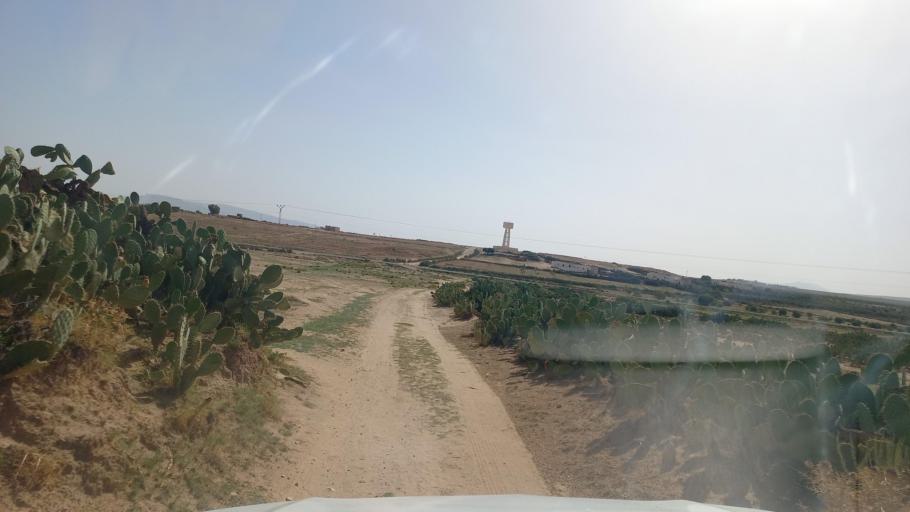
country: TN
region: Al Qasrayn
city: Sbiba
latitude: 35.3161
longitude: 9.0235
